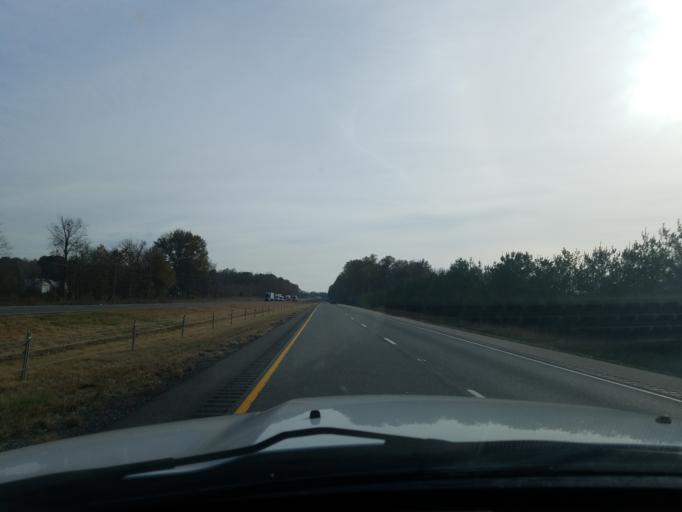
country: US
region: Indiana
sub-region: Jackson County
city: Crothersville
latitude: 38.8698
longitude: -85.8102
